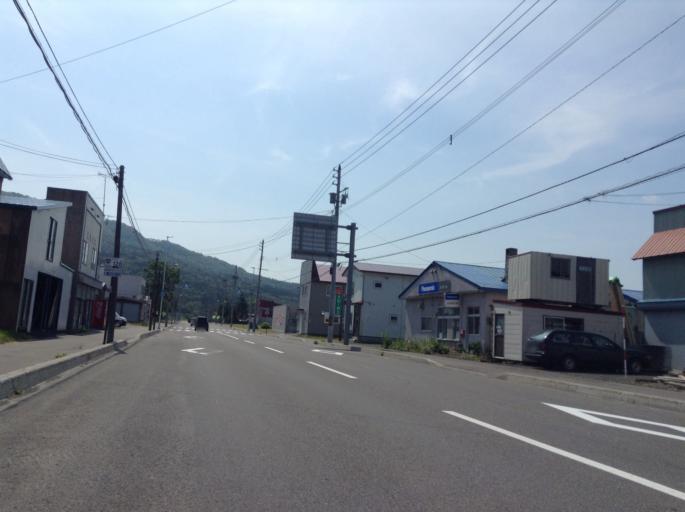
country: JP
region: Hokkaido
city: Nayoro
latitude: 44.7271
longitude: 142.2601
